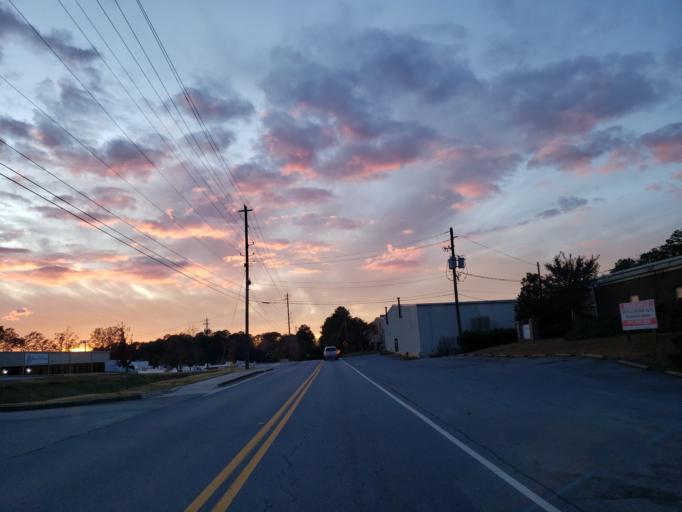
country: US
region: Georgia
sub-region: Bartow County
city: Cartersville
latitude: 34.1900
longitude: -84.7829
